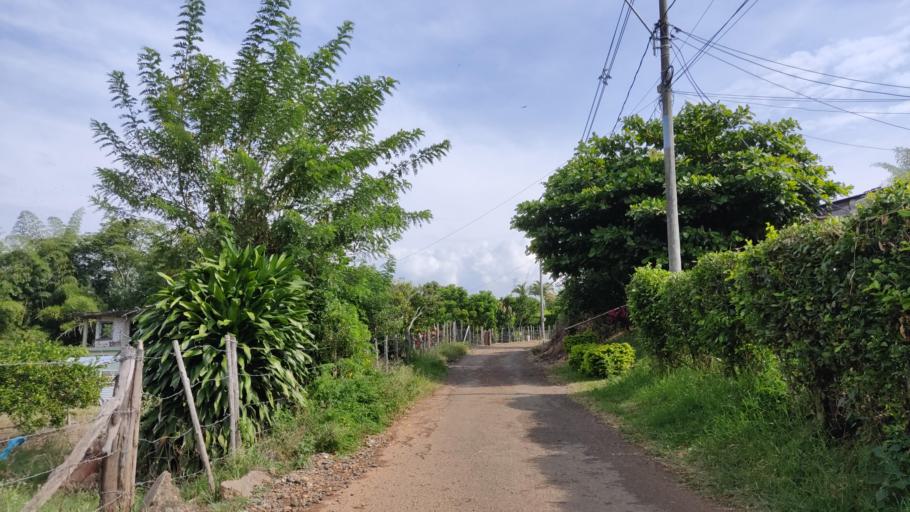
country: CO
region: Cauca
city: Buenos Aires
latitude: 3.1312
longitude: -76.5939
